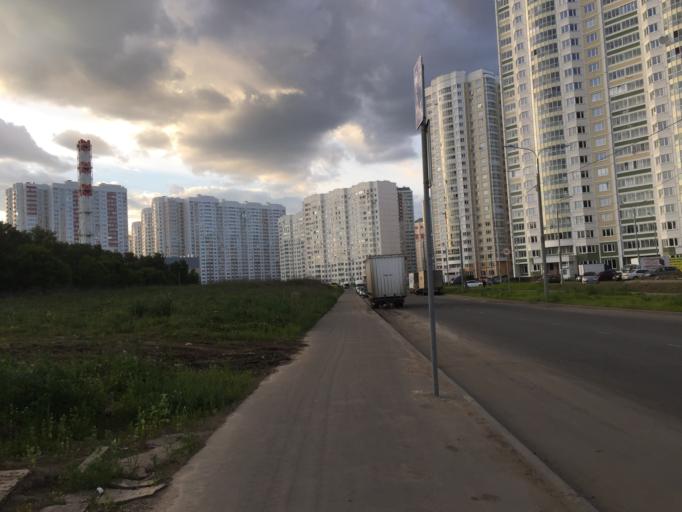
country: RU
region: Moscow
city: Nekrasovka
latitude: 55.6835
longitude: 37.9103
